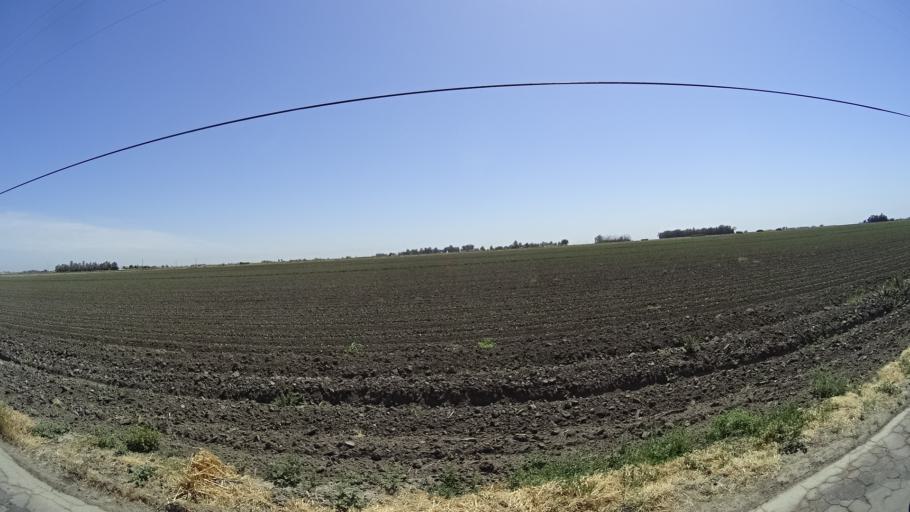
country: US
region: California
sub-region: Kings County
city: Stratford
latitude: 36.2017
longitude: -119.8161
